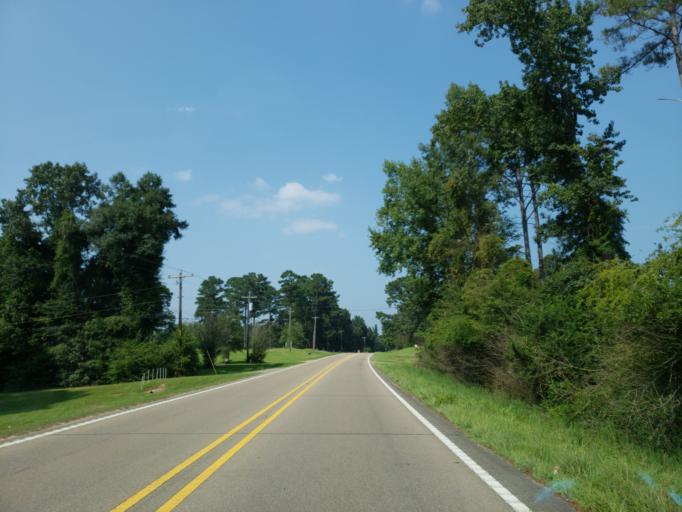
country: US
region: Mississippi
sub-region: Jones County
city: Sharon
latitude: 31.7377
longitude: -89.0841
